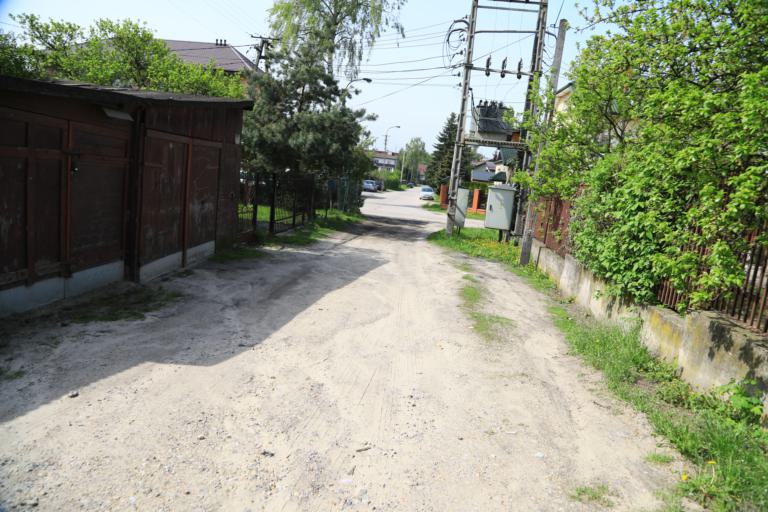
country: PL
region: Masovian Voivodeship
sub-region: Powiat wolominski
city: Wolomin
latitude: 52.3394
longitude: 21.2285
